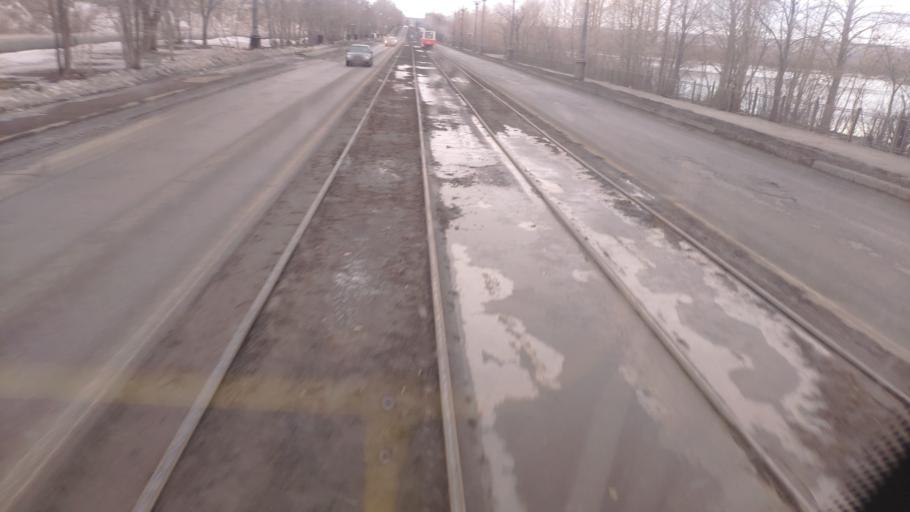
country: RU
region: Chelyabinsk
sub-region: Gorod Magnitogorsk
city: Magnitogorsk
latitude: 53.4222
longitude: 59.0181
